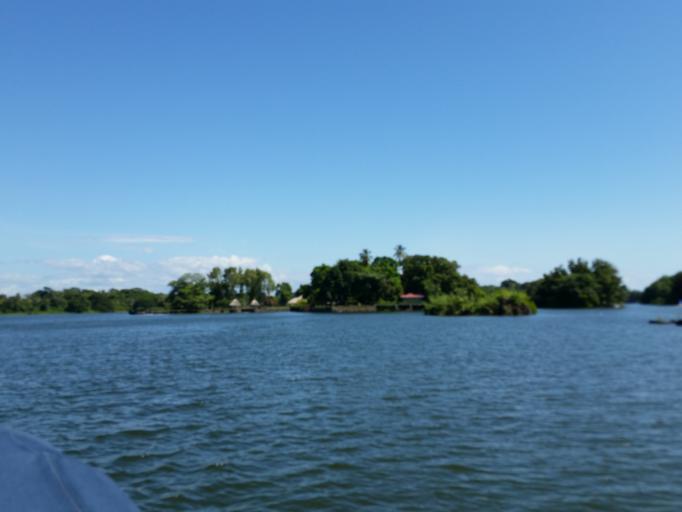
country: NI
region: Granada
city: Granada
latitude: 11.8773
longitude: -85.9029
